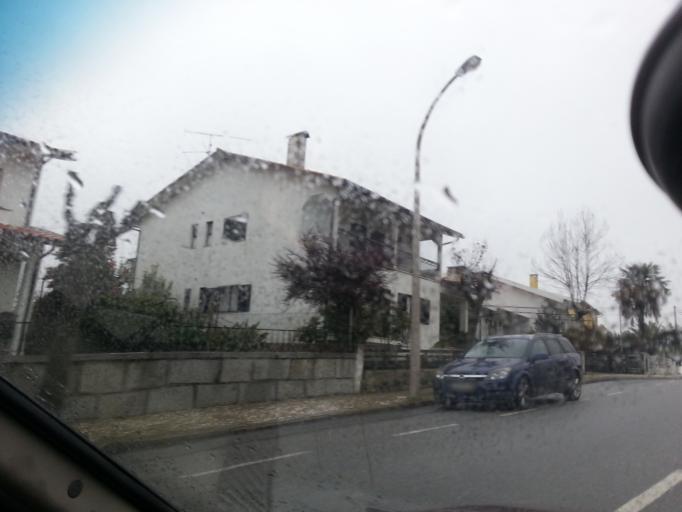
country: PT
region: Viseu
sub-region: Viseu
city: Rio de Loba
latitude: 40.6601
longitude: -7.8762
